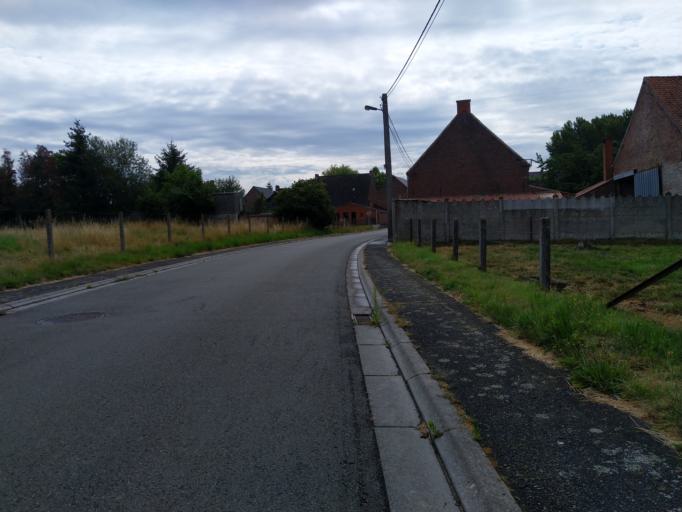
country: BE
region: Wallonia
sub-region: Province du Hainaut
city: Beloeil
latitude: 50.5299
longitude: 3.7417
